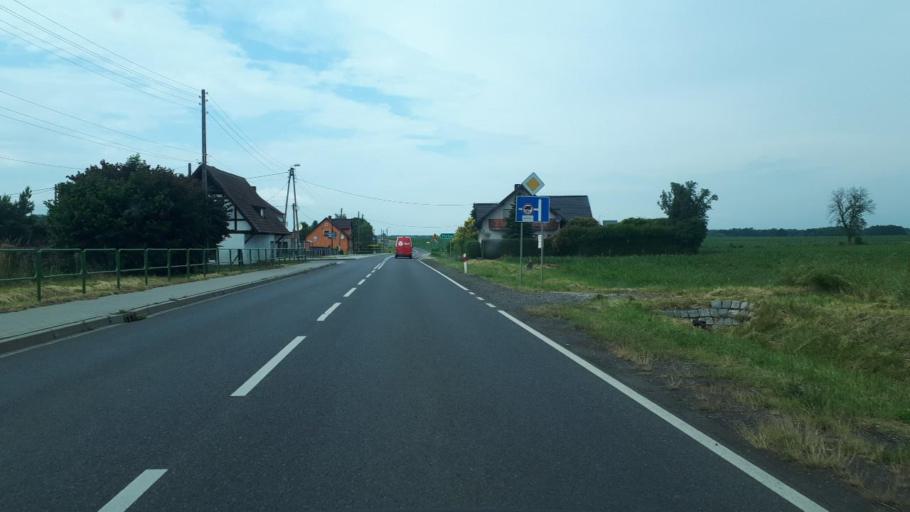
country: PL
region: Silesian Voivodeship
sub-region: Powiat gliwicki
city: Pyskowice
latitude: 50.4190
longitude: 18.6146
